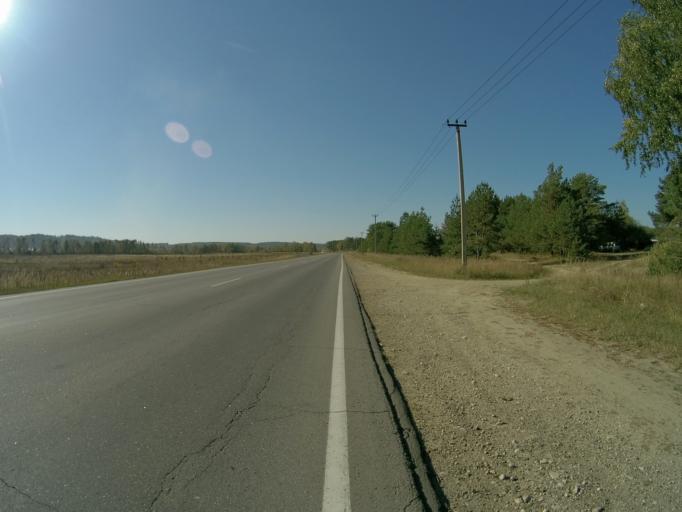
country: RU
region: Vladimir
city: Raduzhnyy
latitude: 56.0310
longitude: 40.3451
